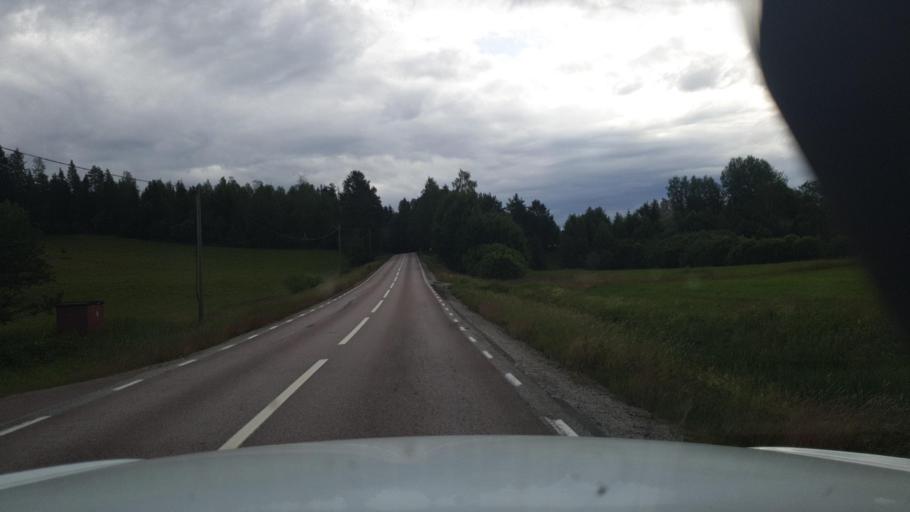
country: SE
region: Vaermland
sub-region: Sunne Kommun
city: Sunne
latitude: 59.6679
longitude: 13.0129
